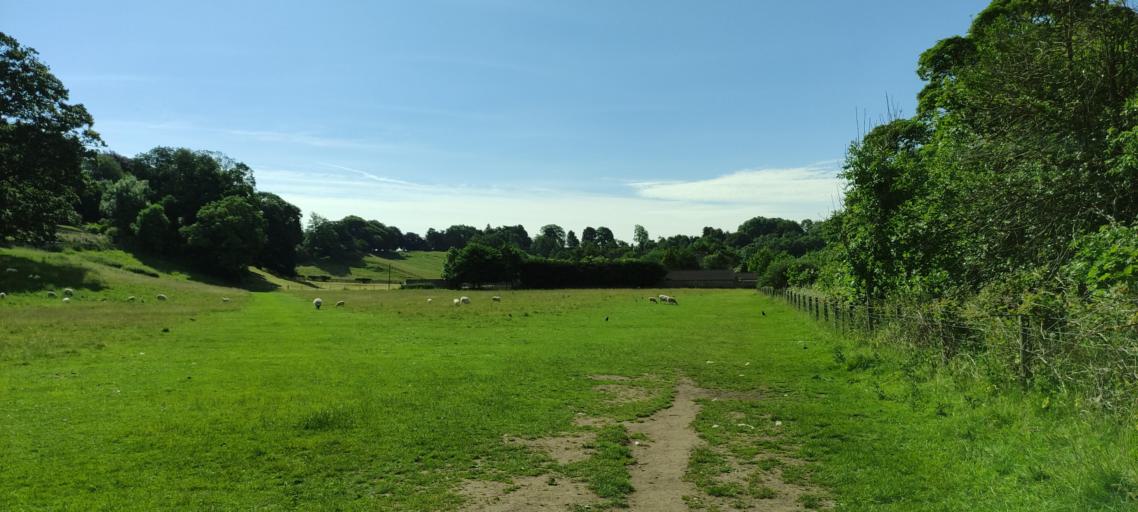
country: GB
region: England
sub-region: North Yorkshire
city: Catterick Garrison
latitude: 54.3997
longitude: -1.7194
